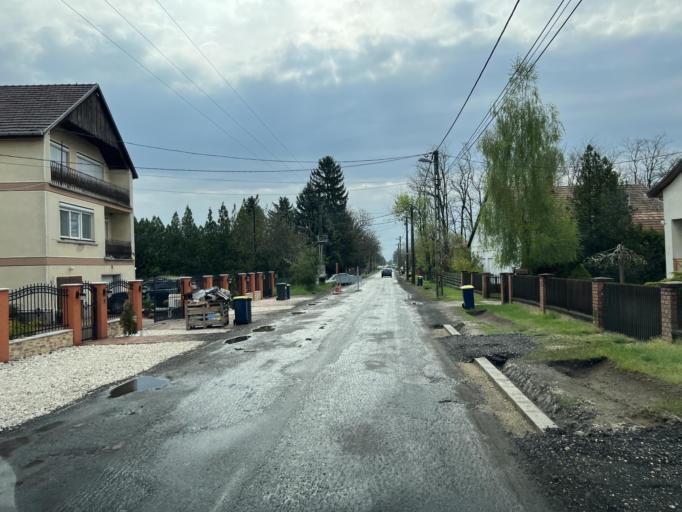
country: HU
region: Pest
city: Danszentmiklos
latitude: 47.2174
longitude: 19.5338
